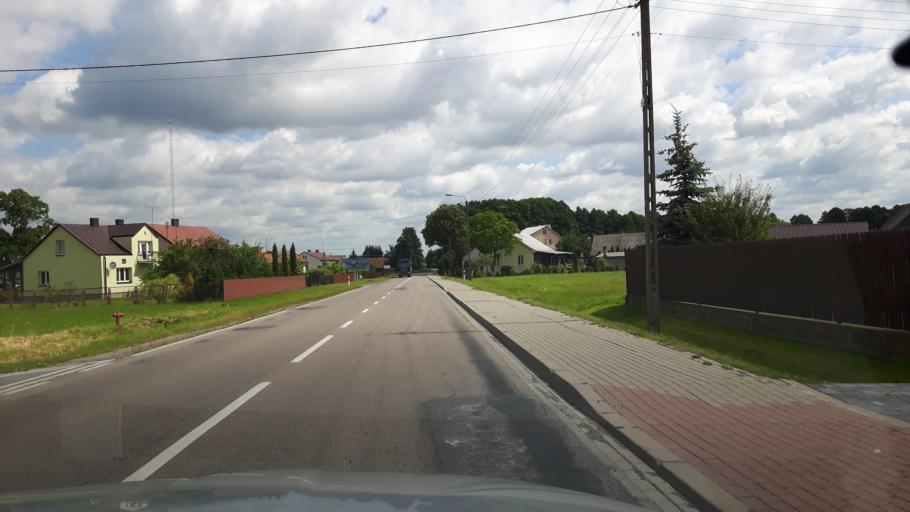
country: PL
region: Masovian Voivodeship
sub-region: Powiat ostrowski
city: Brok
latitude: 52.7033
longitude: 21.8819
